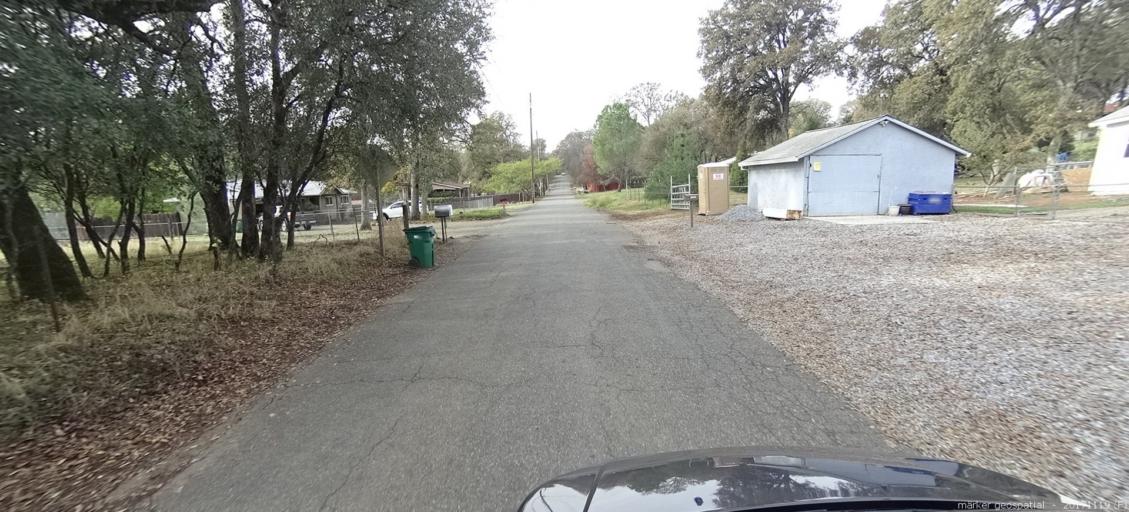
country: US
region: California
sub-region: Shasta County
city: Anderson
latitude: 40.4766
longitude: -122.2963
